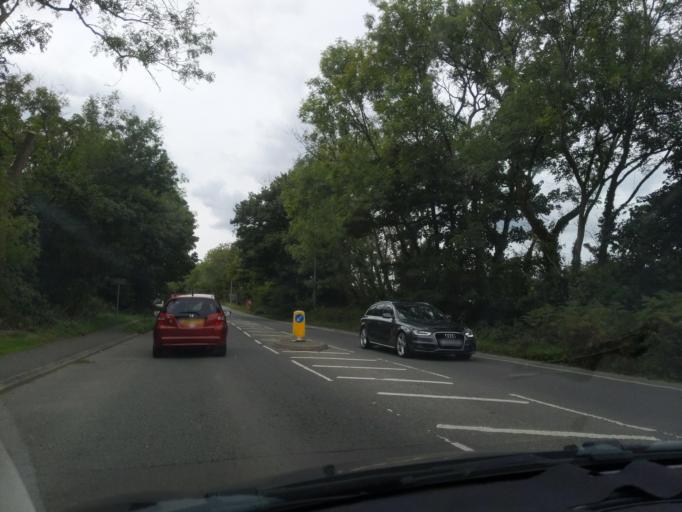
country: GB
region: England
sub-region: Cornwall
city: St Austell
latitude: 50.3421
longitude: -4.7520
